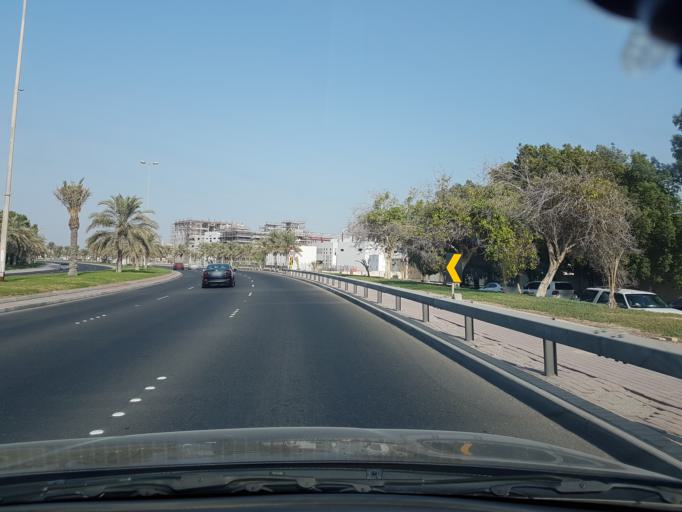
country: BH
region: Muharraq
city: Al Muharraq
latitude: 26.2425
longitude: 50.6151
